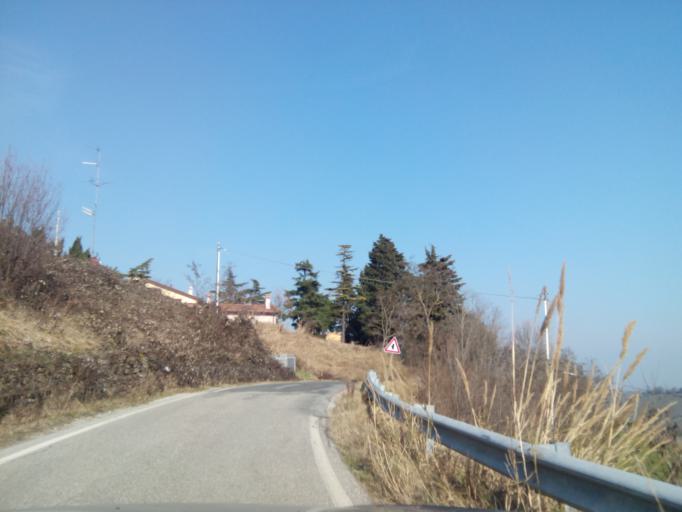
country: IT
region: Emilia-Romagna
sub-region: Provincia di Ravenna
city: Riolo Terme
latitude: 44.3092
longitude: 11.6865
